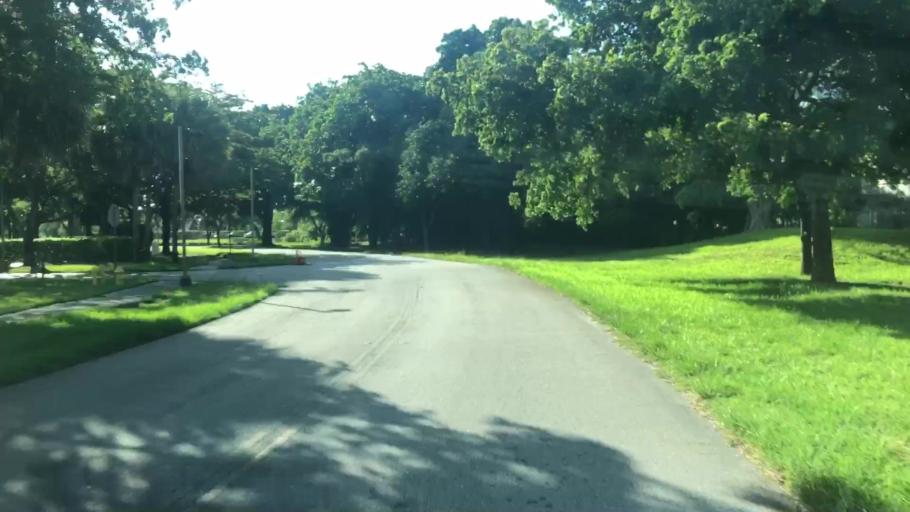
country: US
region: Florida
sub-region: Broward County
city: Kendall Green
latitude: 26.2639
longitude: -80.1441
